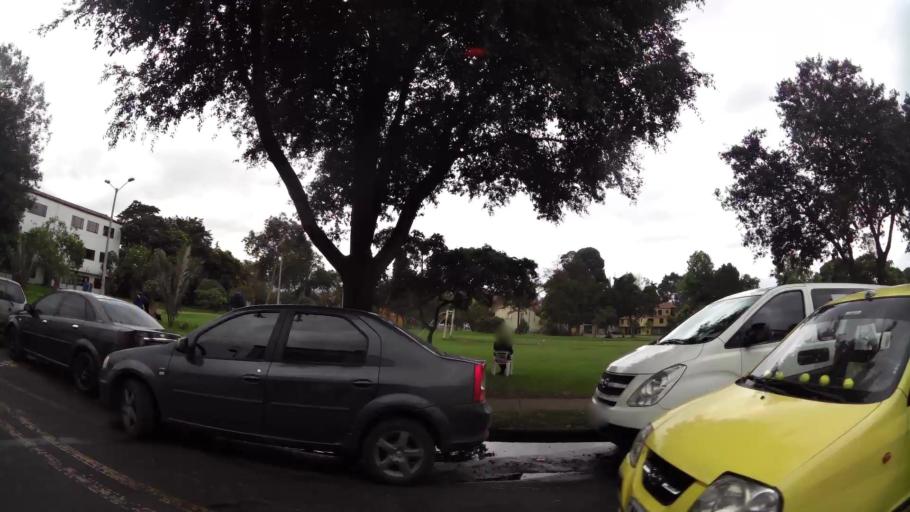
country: CO
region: Bogota D.C.
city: Bogota
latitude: 4.6657
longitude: -74.1178
